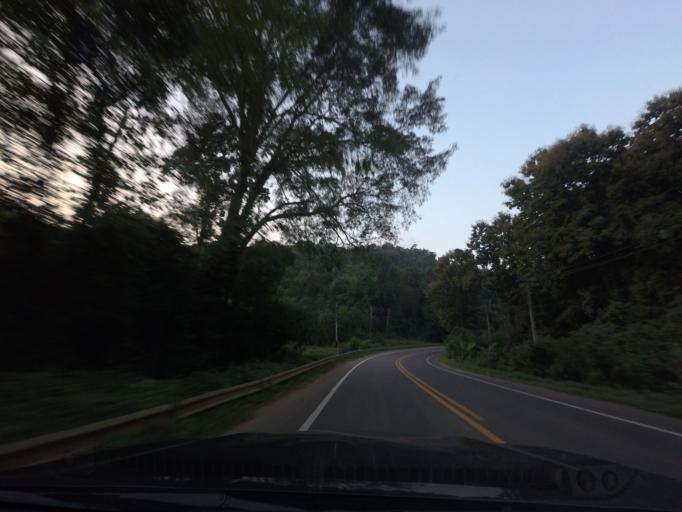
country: TH
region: Nan
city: Na Noi
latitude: 18.4412
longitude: 100.7084
